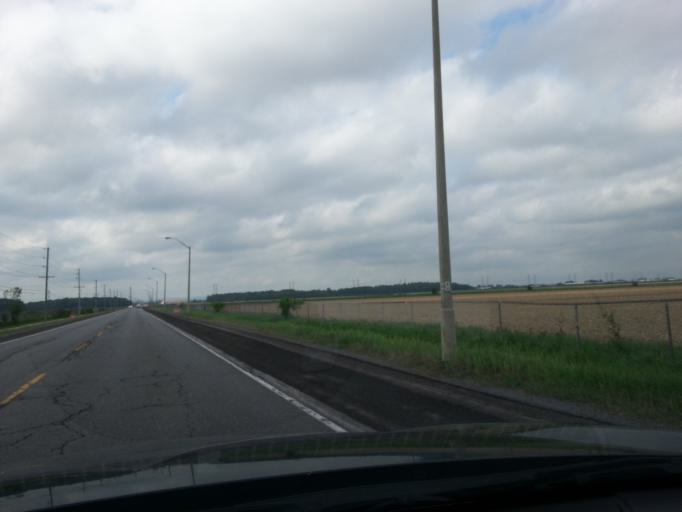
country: CA
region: Ontario
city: Bells Corners
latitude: 45.3020
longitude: -75.7653
